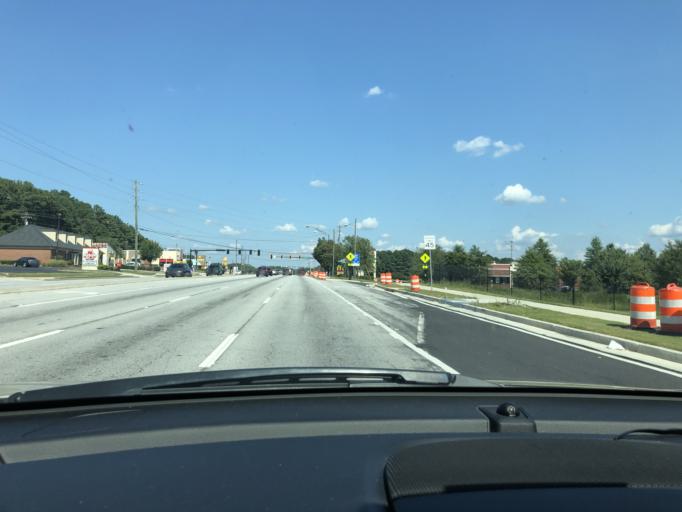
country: US
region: Georgia
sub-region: Gwinnett County
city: Snellville
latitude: 33.8555
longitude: -84.0267
